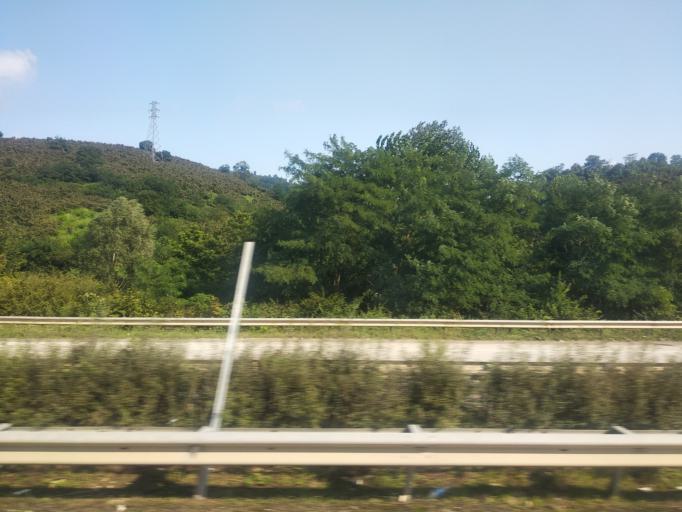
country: TR
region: Ordu
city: Ordu
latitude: 40.9951
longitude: 37.8181
